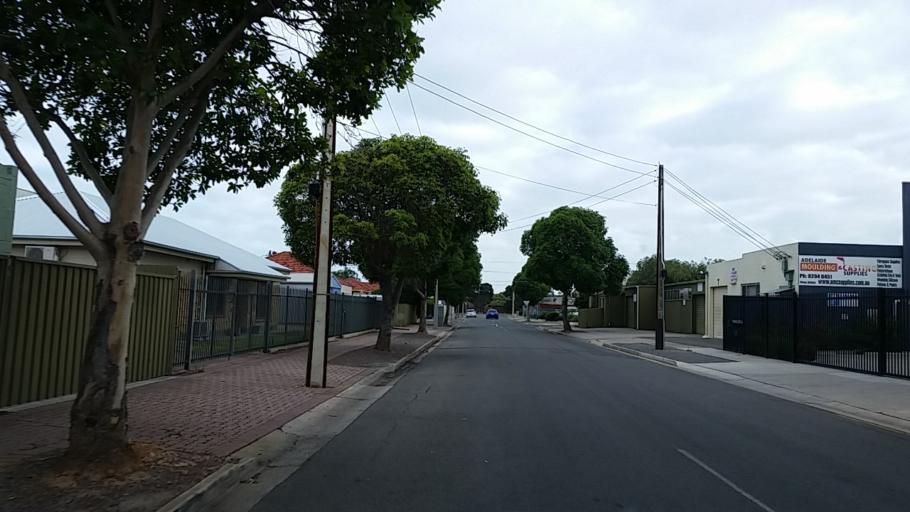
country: AU
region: South Australia
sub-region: Holdfast Bay
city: North Brighton
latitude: -34.9988
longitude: 138.5243
